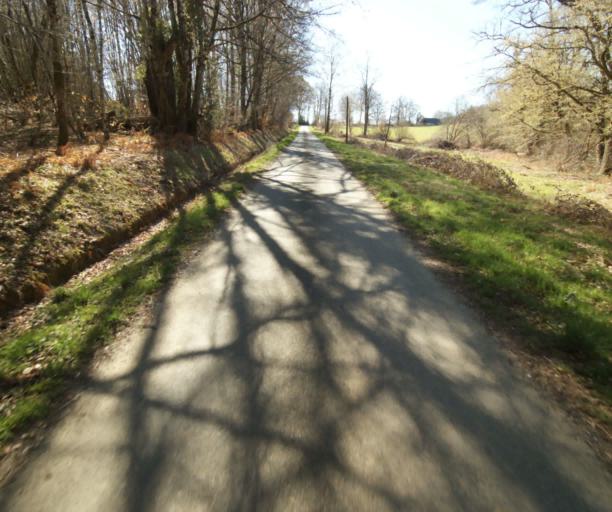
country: FR
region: Limousin
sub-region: Departement de la Correze
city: Seilhac
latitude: 45.4039
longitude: 1.7347
